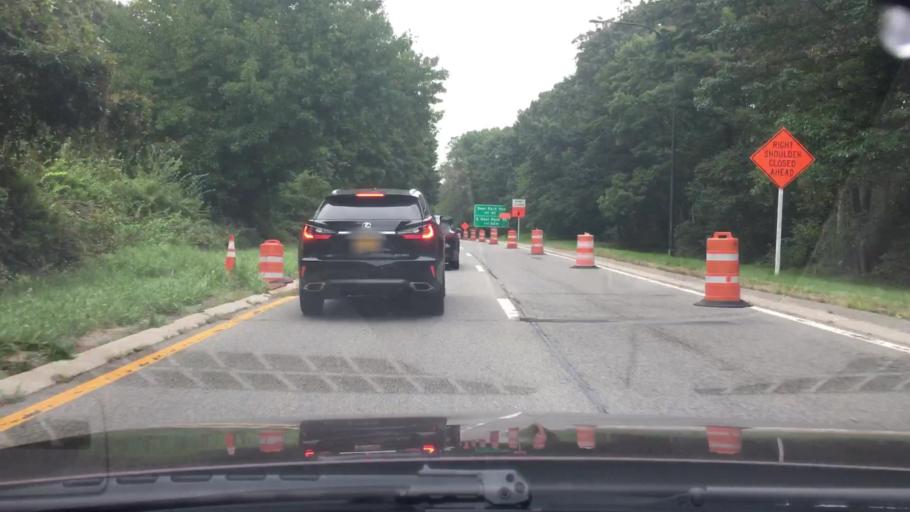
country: US
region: New York
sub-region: Suffolk County
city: Dix Hills
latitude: 40.8243
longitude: -73.3546
